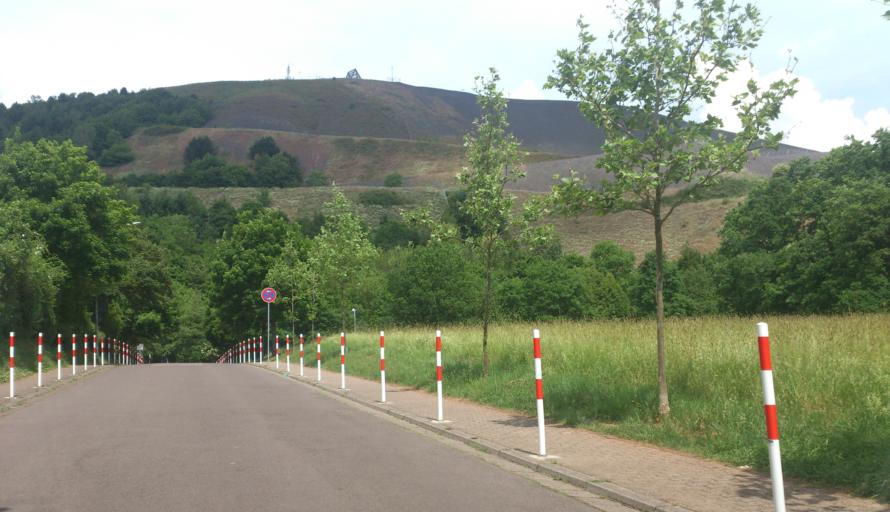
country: DE
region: Saarland
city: Ensdorf
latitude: 49.3138
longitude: 6.7866
